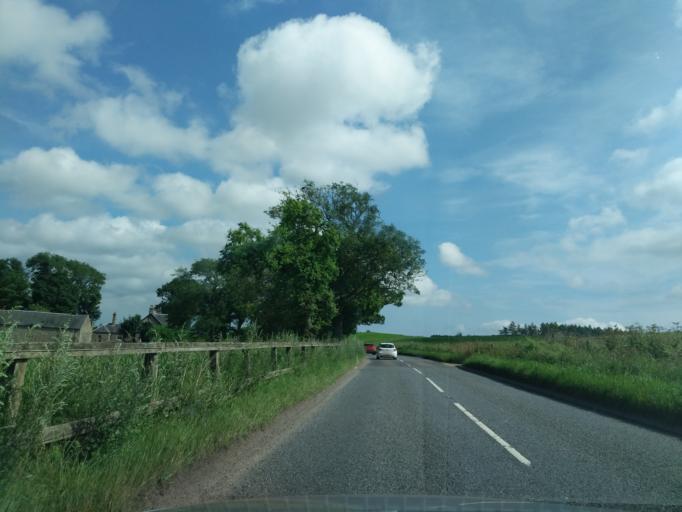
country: GB
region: Scotland
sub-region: Angus
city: Muirhead
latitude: 56.5070
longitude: -3.1503
